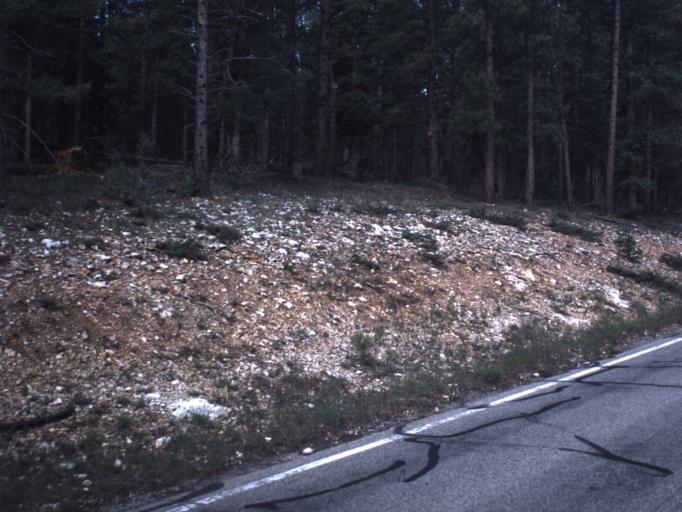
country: US
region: Utah
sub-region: Garfield County
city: Panguitch
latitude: 37.5116
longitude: -112.6325
